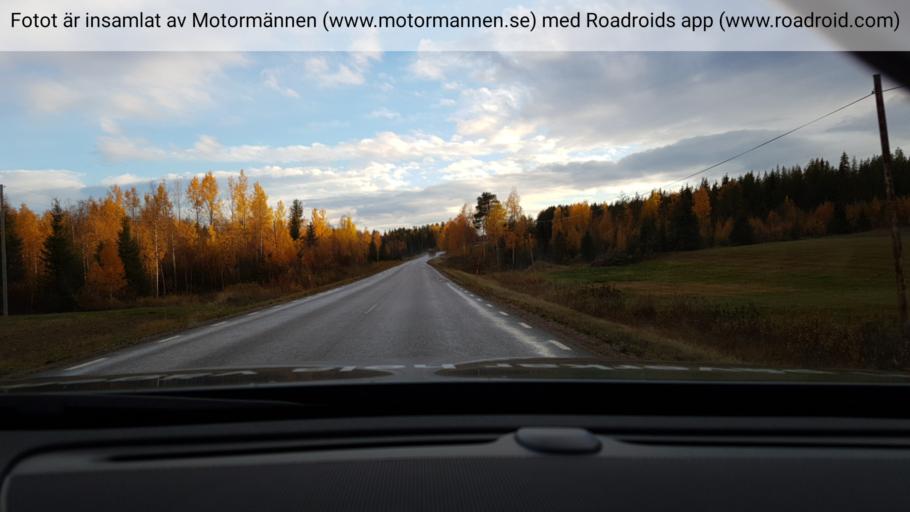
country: SE
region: Norrbotten
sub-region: Overkalix Kommun
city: OEverkalix
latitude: 66.7374
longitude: 22.6695
